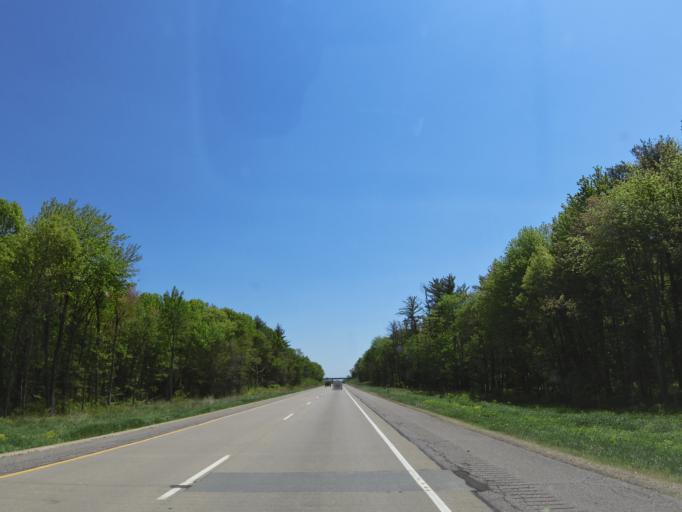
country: US
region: Wisconsin
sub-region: Juneau County
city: New Lisbon
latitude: 43.8666
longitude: -90.1214
